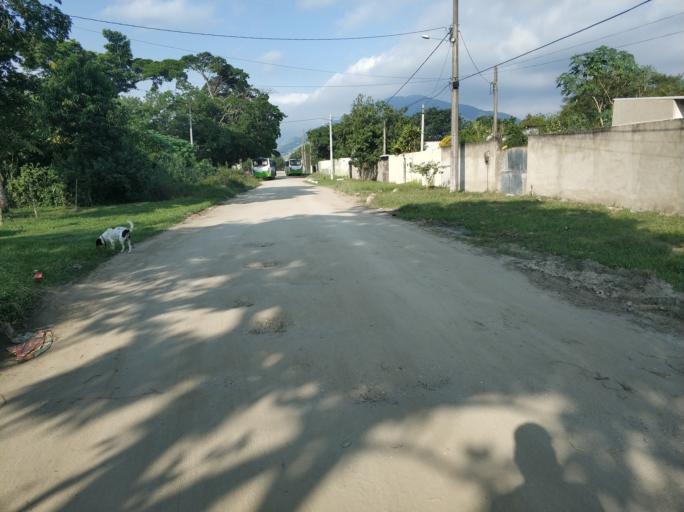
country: BR
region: Rio de Janeiro
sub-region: Seropedica
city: Seropedica
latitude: -22.8228
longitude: -43.6362
